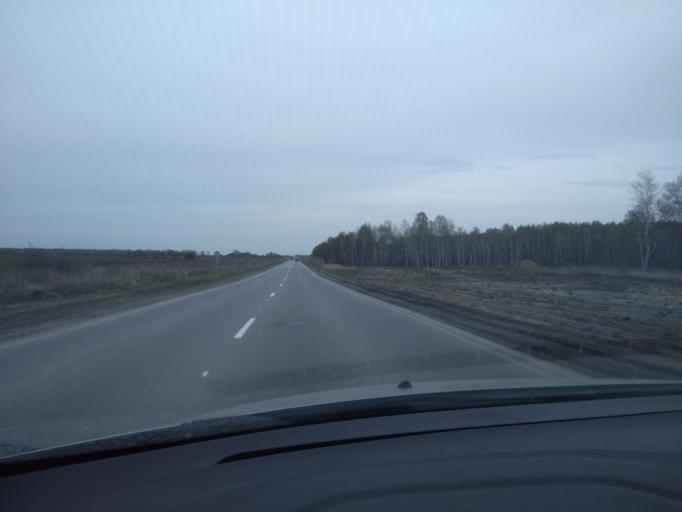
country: RU
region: Sverdlovsk
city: Pyshma
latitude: 56.8907
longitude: 63.0330
